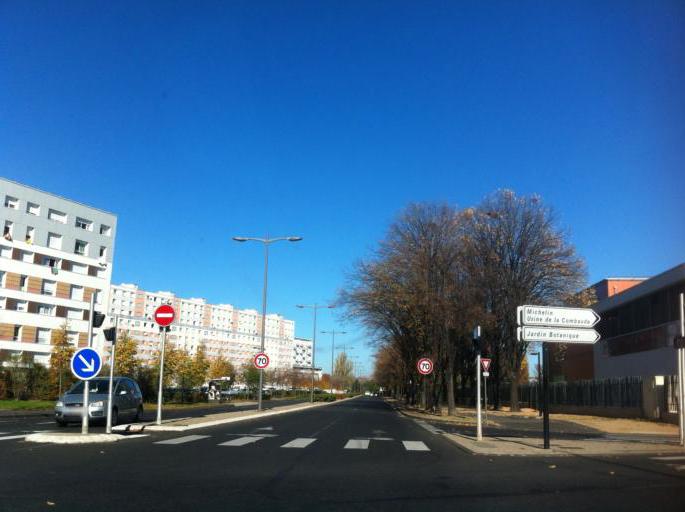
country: FR
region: Auvergne
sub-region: Departement du Puy-de-Dome
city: Aulnat
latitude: 45.7981
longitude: 3.1504
